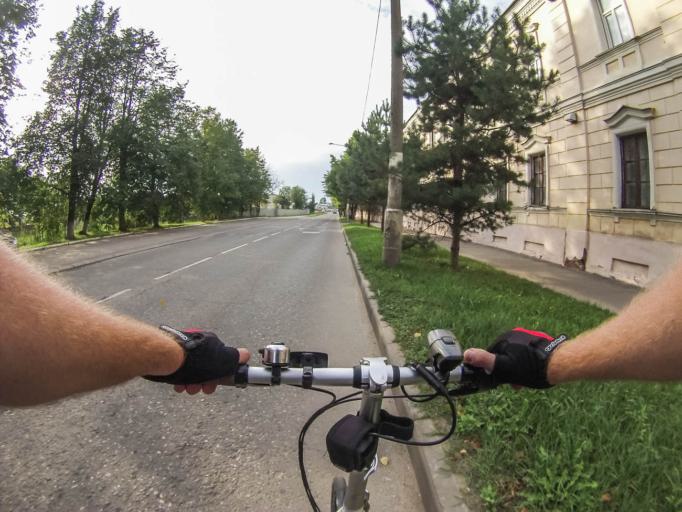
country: RU
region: Kostroma
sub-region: Kostromskoy Rayon
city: Kostroma
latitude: 57.7668
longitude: 40.9179
